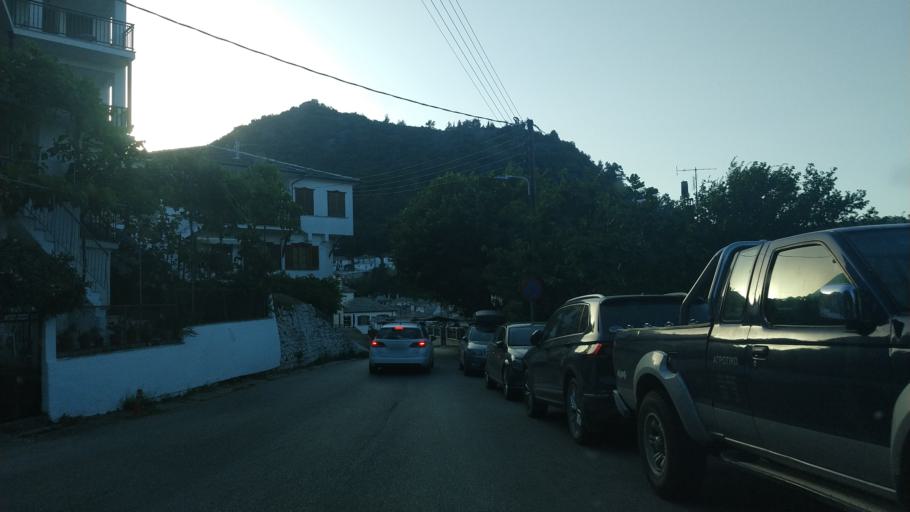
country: GR
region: East Macedonia and Thrace
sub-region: Nomos Kavalas
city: Potamia
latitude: 40.7300
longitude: 24.7306
